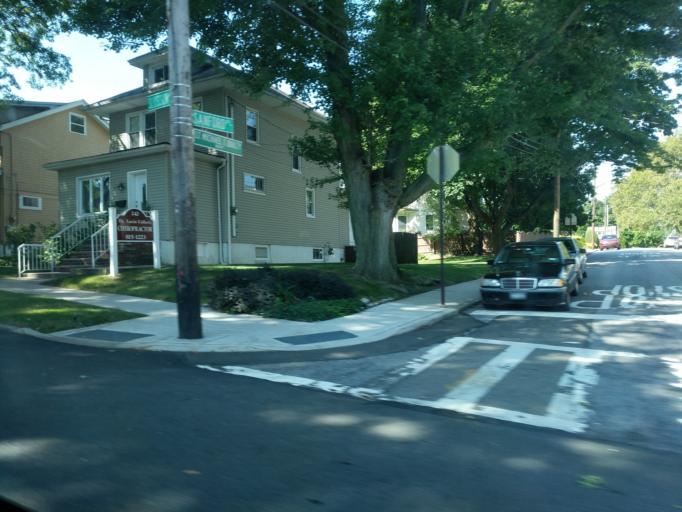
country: US
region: New Jersey
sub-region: Hudson County
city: Bayonne
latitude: 40.6150
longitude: -74.1170
